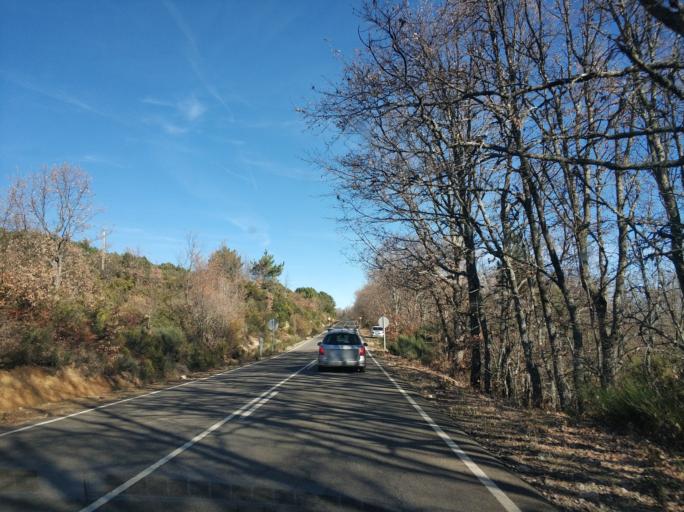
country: ES
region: Castille and Leon
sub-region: Provincia de Salamanca
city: San Miguel de Valero
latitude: 40.5586
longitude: -5.9126
